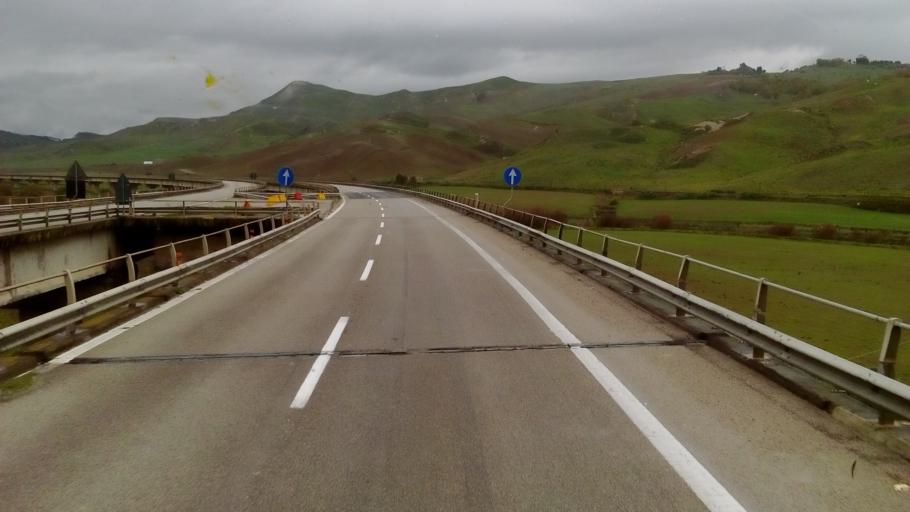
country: IT
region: Sicily
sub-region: Enna
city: Villarosa
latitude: 37.5620
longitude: 14.1976
